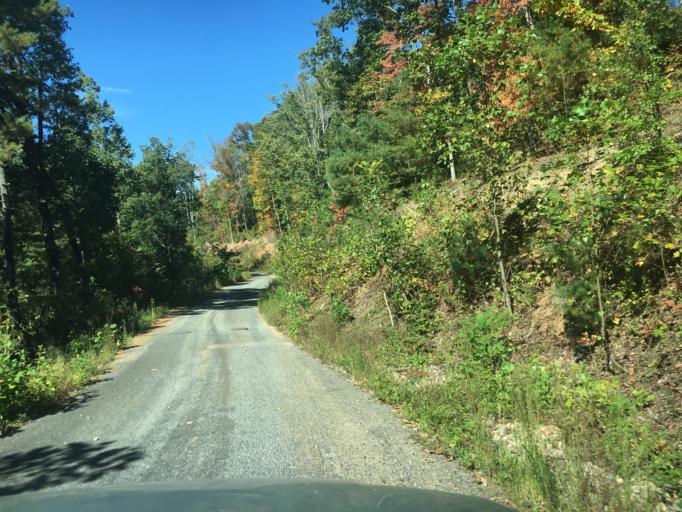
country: US
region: North Carolina
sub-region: Buncombe County
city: Woodfin
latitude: 35.6486
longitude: -82.5890
